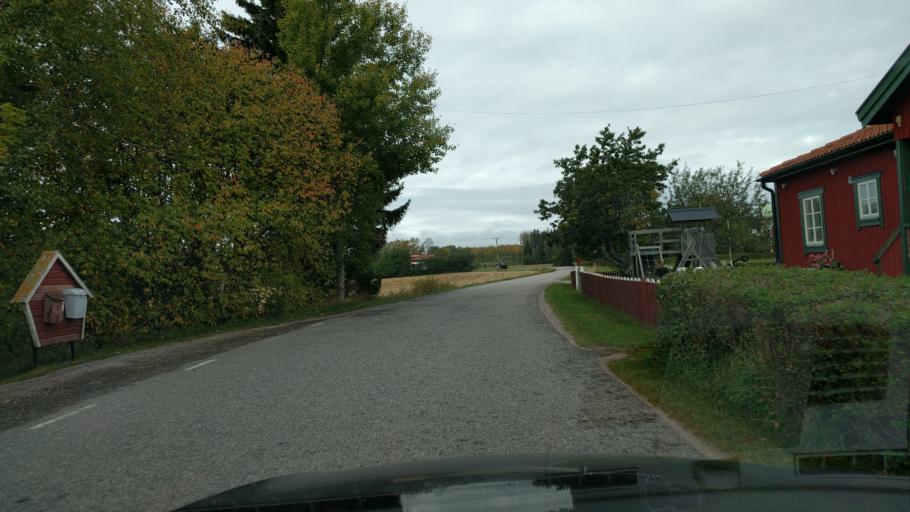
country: SE
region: Uppsala
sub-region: Osthammars Kommun
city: Bjorklinge
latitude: 60.1576
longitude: 17.5433
